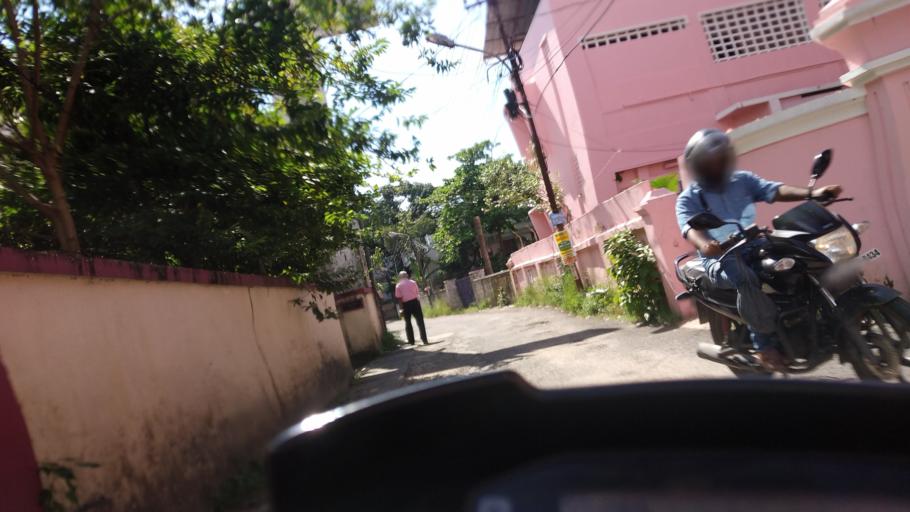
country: IN
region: Kerala
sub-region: Ernakulam
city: Cochin
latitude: 9.9761
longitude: 76.2829
